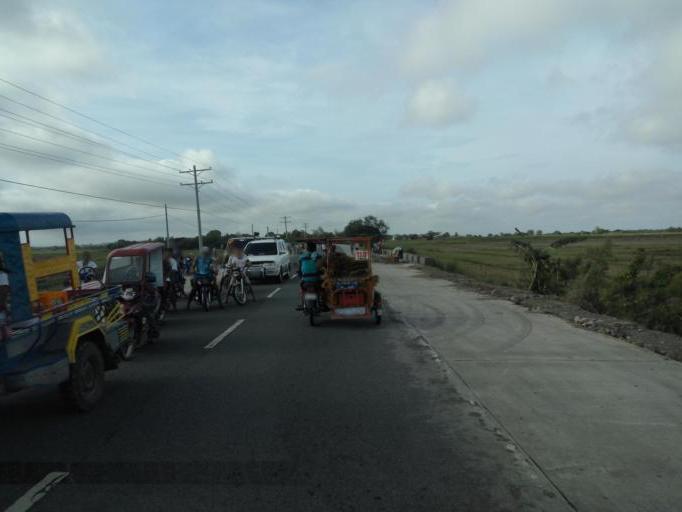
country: PH
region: Cagayan Valley
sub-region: Province of Isabela
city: Cabagan
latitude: 17.4090
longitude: 121.8053
